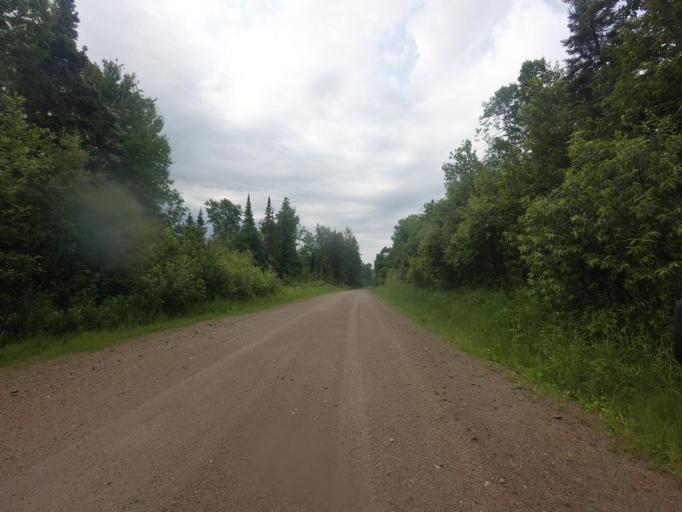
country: CA
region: Quebec
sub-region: Outaouais
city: Maniwaki
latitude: 46.3284
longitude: -76.0045
